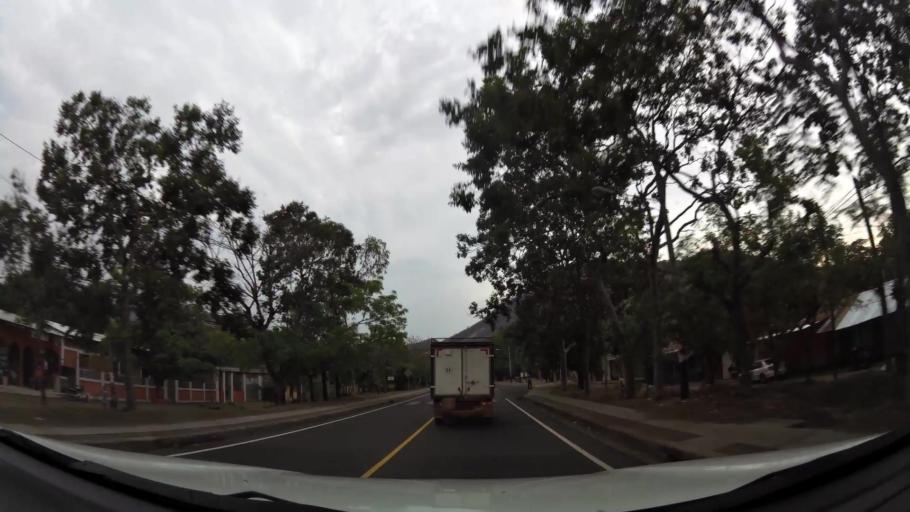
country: NI
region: Matagalpa
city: Ciudad Dario
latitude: 12.9316
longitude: -86.1986
